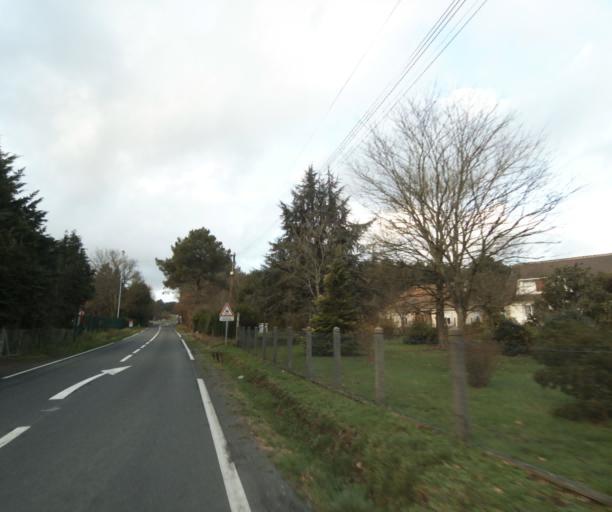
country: FR
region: Pays de la Loire
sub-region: Departement de la Sarthe
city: Ruaudin
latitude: 47.9661
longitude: 0.2400
